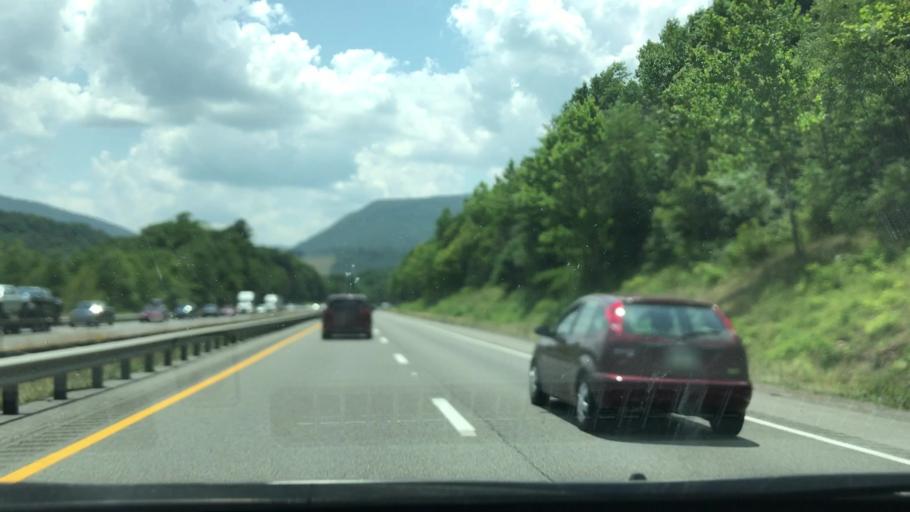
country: US
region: West Virginia
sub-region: Mercer County
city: Bluefield
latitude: 37.2511
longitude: -81.1162
